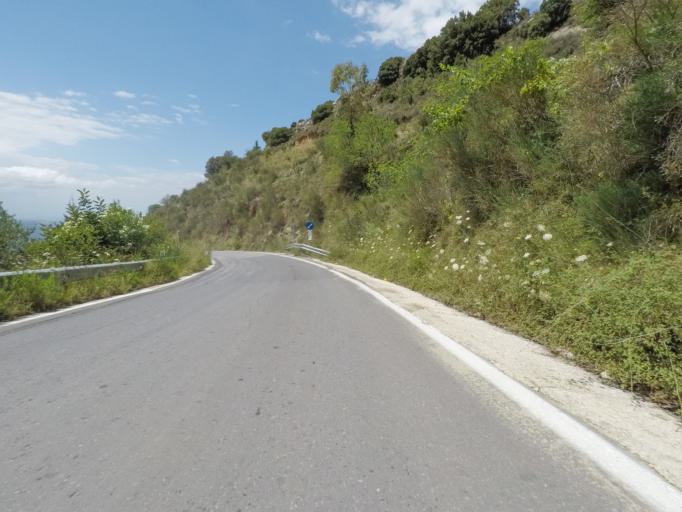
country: GR
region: Crete
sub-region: Nomos Irakleiou
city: Mokhos
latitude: 35.2133
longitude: 25.4613
